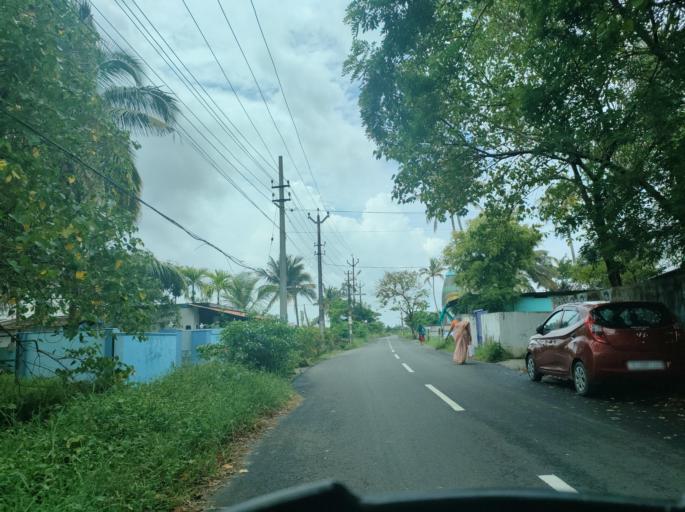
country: IN
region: Kerala
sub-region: Ernakulam
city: Elur
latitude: 10.0557
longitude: 76.2107
